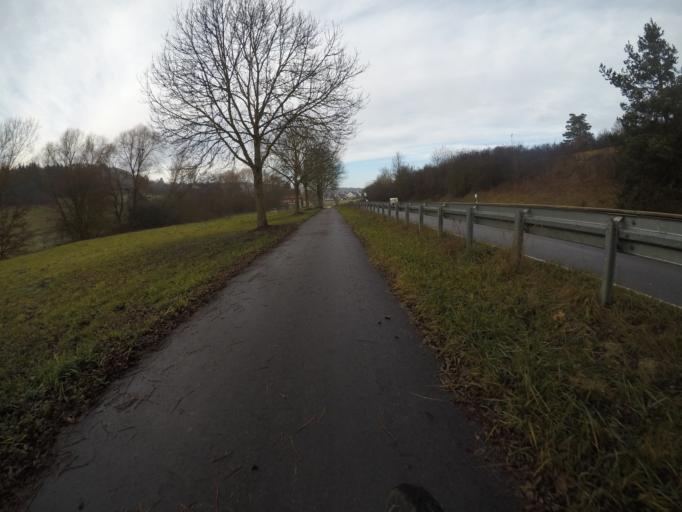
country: DE
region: Baden-Wuerttemberg
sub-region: Regierungsbezirk Stuttgart
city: Aidlingen
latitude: 48.6786
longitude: 8.8633
